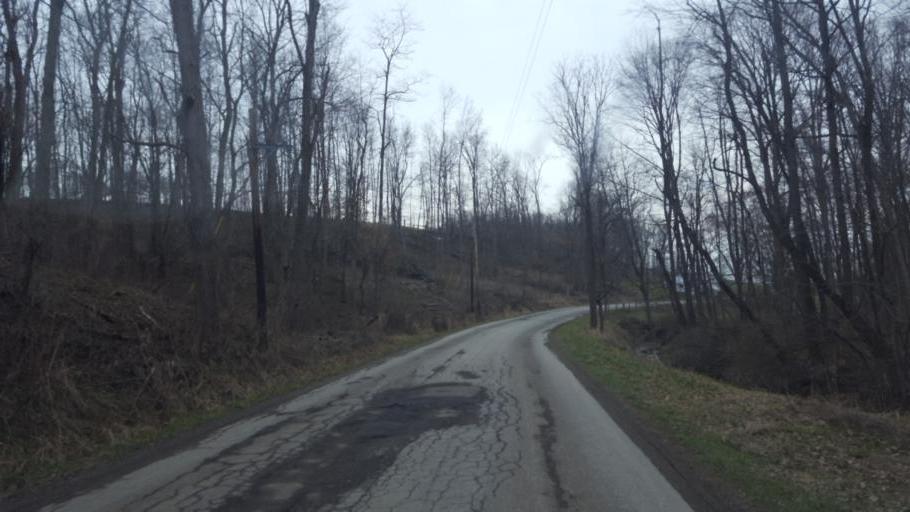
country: US
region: Ohio
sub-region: Tuscarawas County
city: Sugarcreek
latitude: 40.5067
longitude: -81.7357
